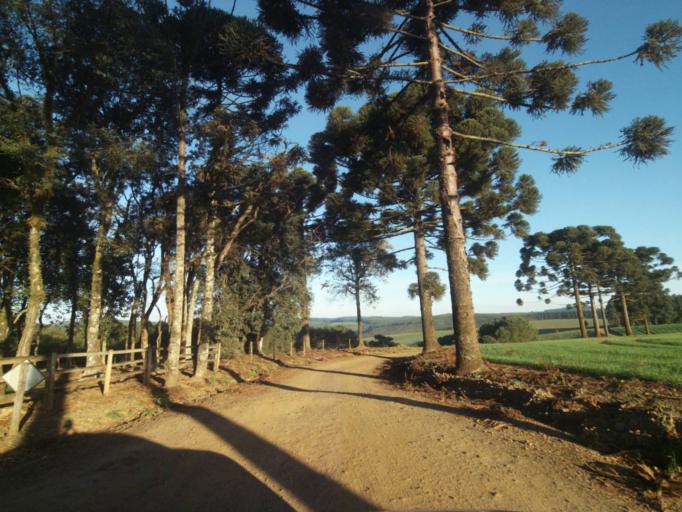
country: BR
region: Parana
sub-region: Telemaco Borba
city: Telemaco Borba
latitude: -24.4728
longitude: -50.5870
